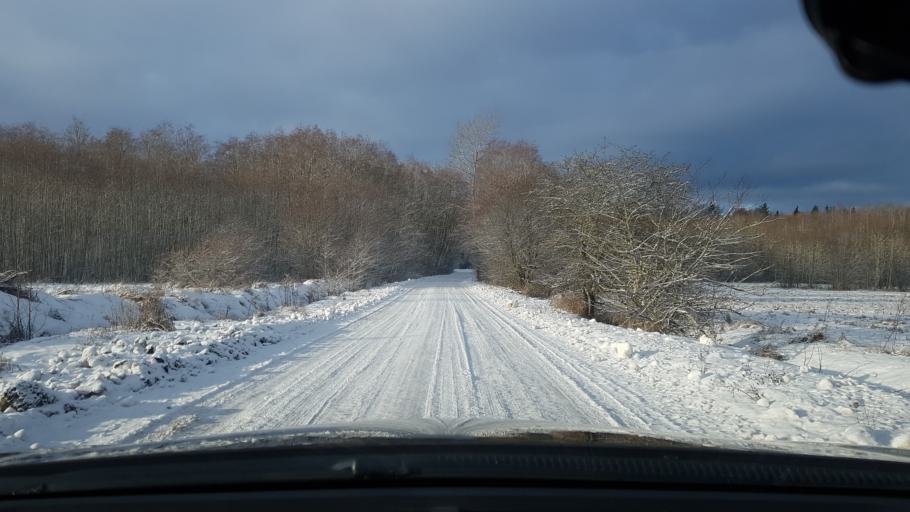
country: EE
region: Harju
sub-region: Keila linn
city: Keila
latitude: 59.3138
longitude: 24.2503
